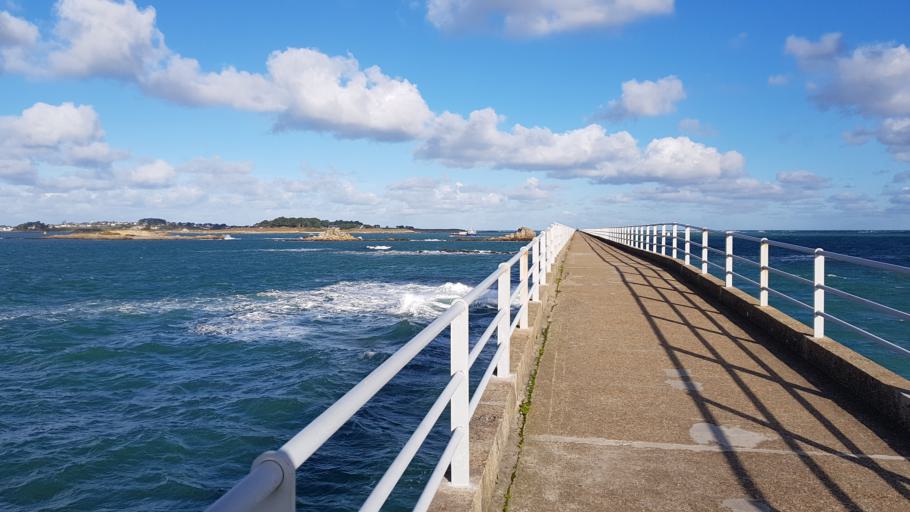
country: FR
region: Brittany
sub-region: Departement du Finistere
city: Roscoff
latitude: 48.7278
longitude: -3.9817
